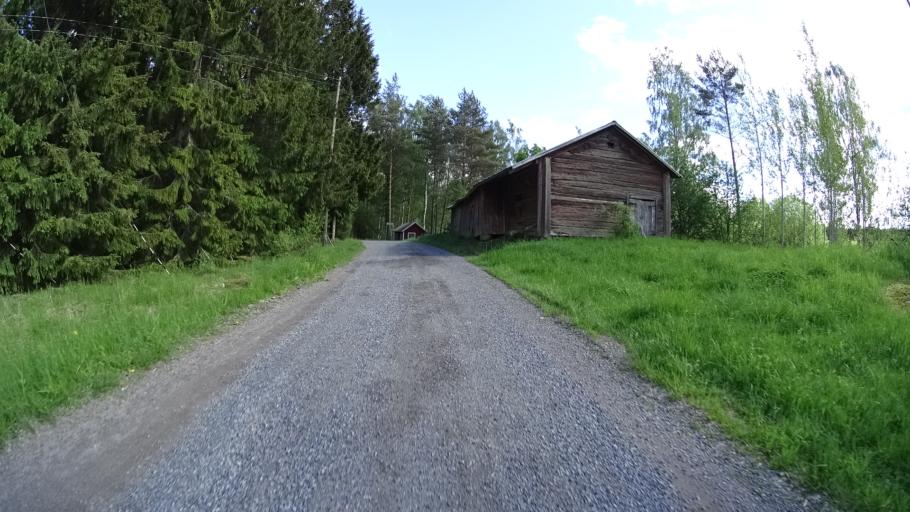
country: FI
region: Varsinais-Suomi
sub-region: Salo
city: Kisko
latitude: 60.1964
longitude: 23.5481
